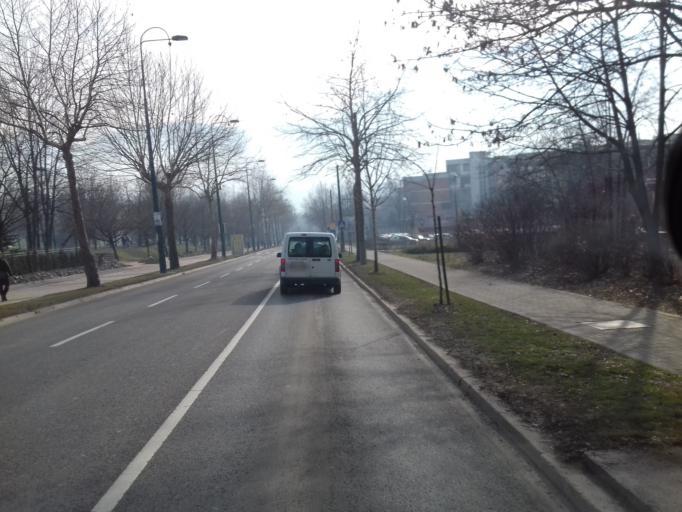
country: BA
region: Federation of Bosnia and Herzegovina
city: Kobilja Glava
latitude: 43.8659
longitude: 18.4102
